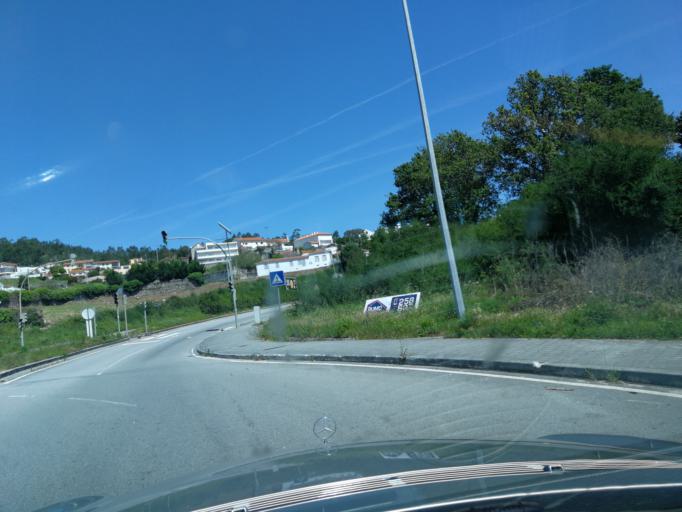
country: PT
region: Viana do Castelo
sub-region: Viana do Castelo
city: Meadela
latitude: 41.7111
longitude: -8.8116
